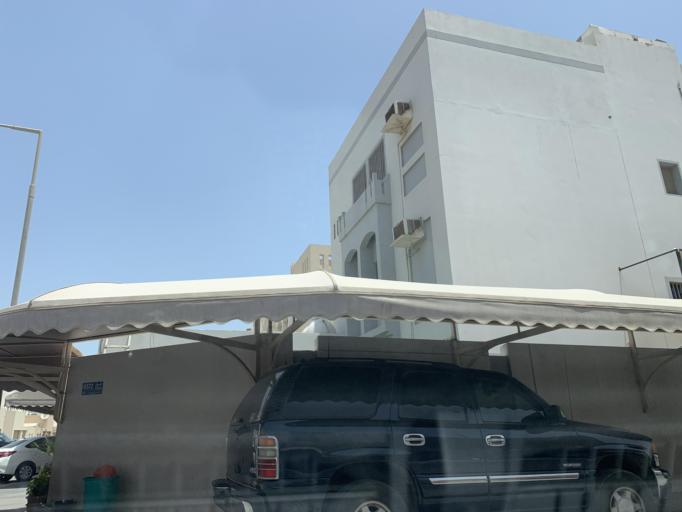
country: BH
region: Northern
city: Sitrah
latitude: 26.1402
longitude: 50.5941
